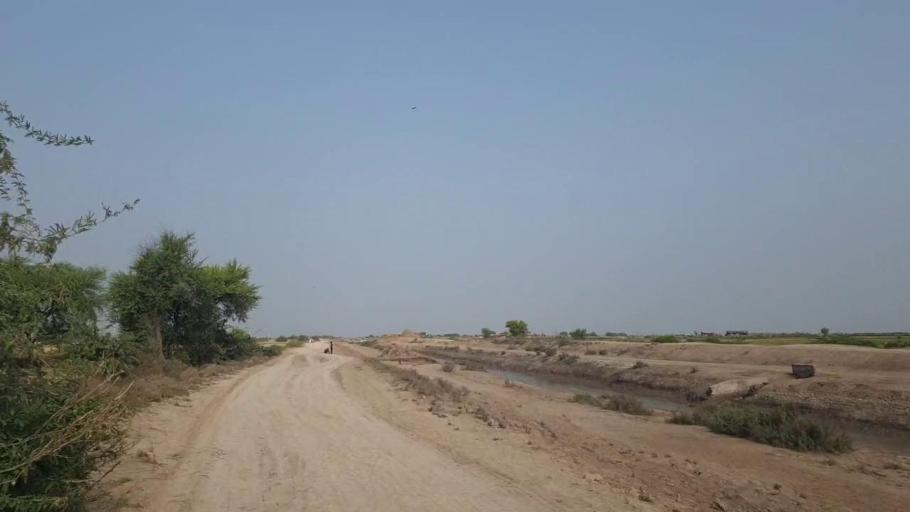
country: PK
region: Sindh
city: Badin
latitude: 24.7080
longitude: 68.7742
